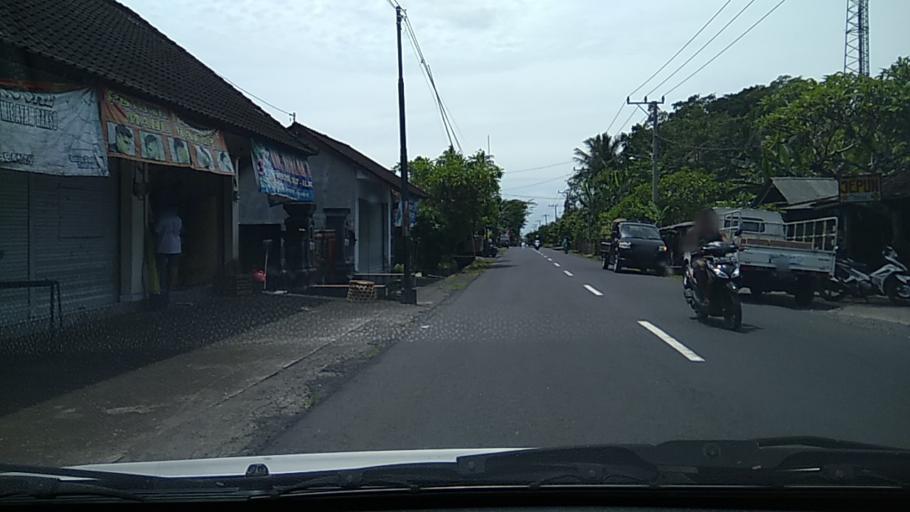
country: ID
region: Bali
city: Wanasari Baleran
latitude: -8.4788
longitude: 115.1361
